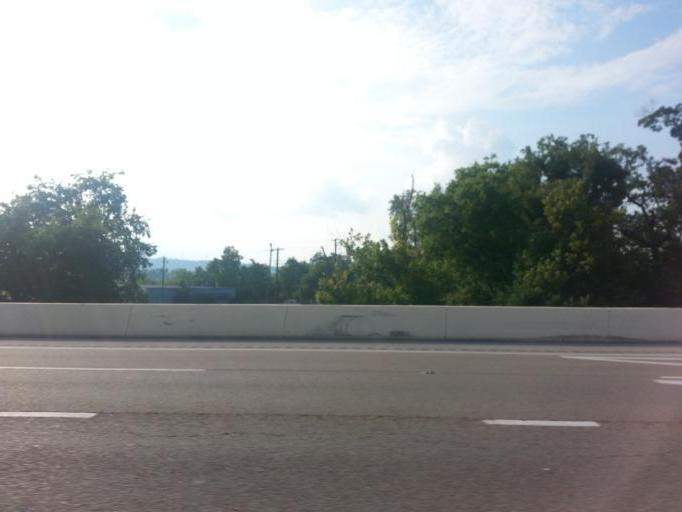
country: US
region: Tennessee
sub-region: Knox County
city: Knoxville
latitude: 35.9883
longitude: -83.9059
